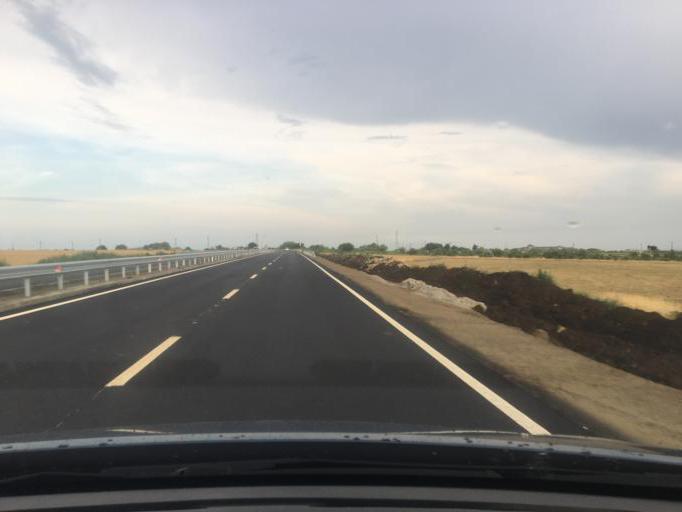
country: BG
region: Burgas
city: Aheloy
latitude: 42.6540
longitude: 27.6614
